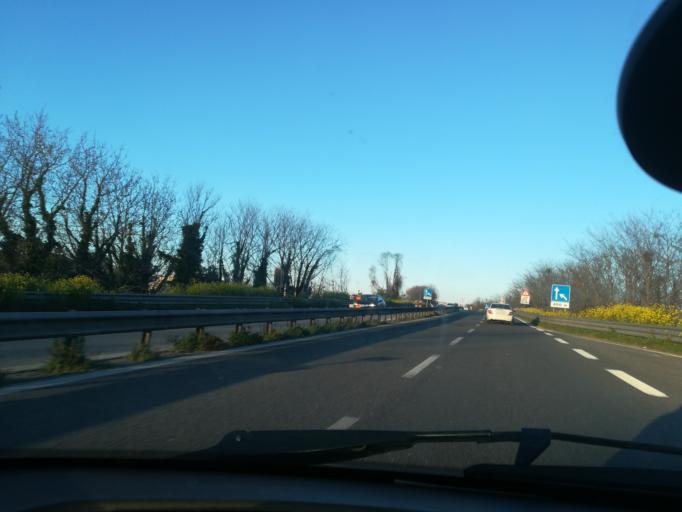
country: IT
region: The Marches
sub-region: Provincia di Macerata
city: Civitanova Marche
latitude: 43.2934
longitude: 13.7190
